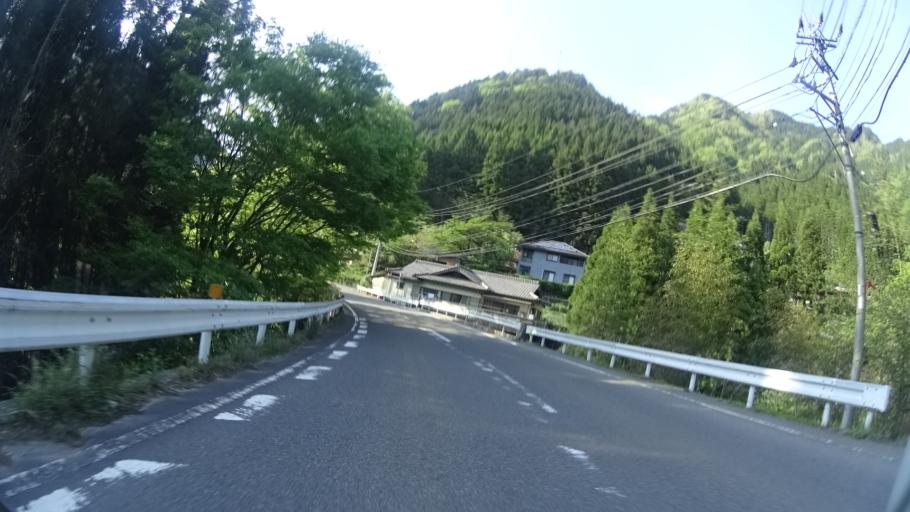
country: JP
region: Tokushima
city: Ikedacho
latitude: 33.8703
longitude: 133.8729
